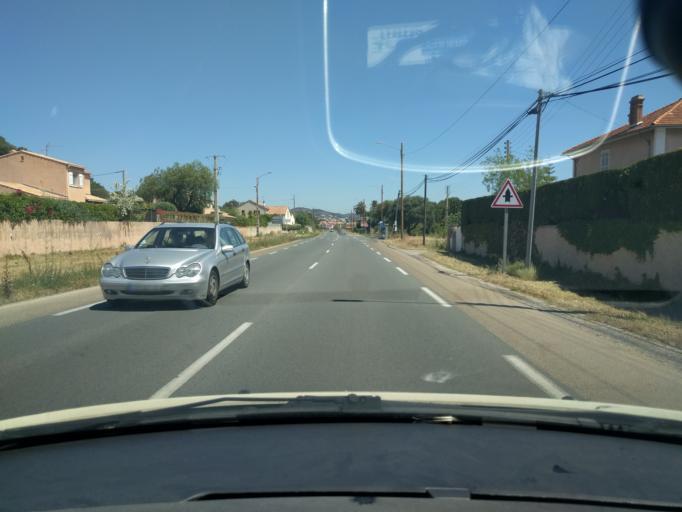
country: FR
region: Provence-Alpes-Cote d'Azur
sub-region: Departement du Var
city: Hyeres
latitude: 43.0931
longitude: 6.1304
